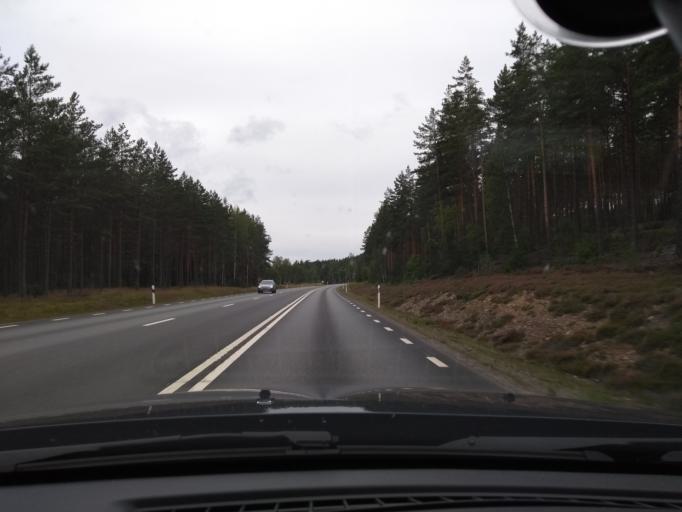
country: SE
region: Joenkoeping
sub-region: Eksjo Kommun
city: Haljarp
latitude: 57.6400
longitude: 15.2964
